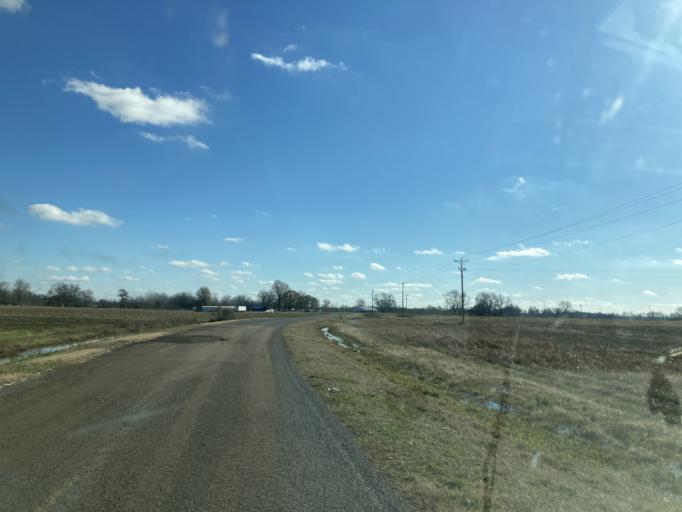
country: US
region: Mississippi
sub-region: Yazoo County
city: Yazoo City
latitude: 32.9302
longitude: -90.4720
